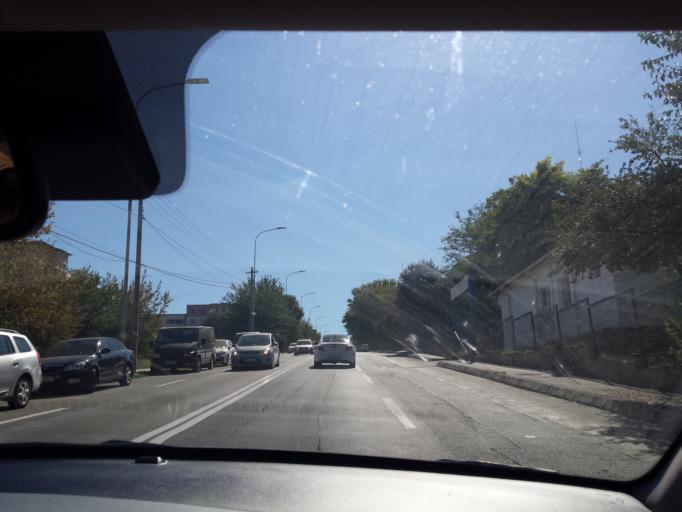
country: RO
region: Tulcea
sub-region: Municipiul Tulcea
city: Tulcea
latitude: 45.1672
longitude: 28.7943
